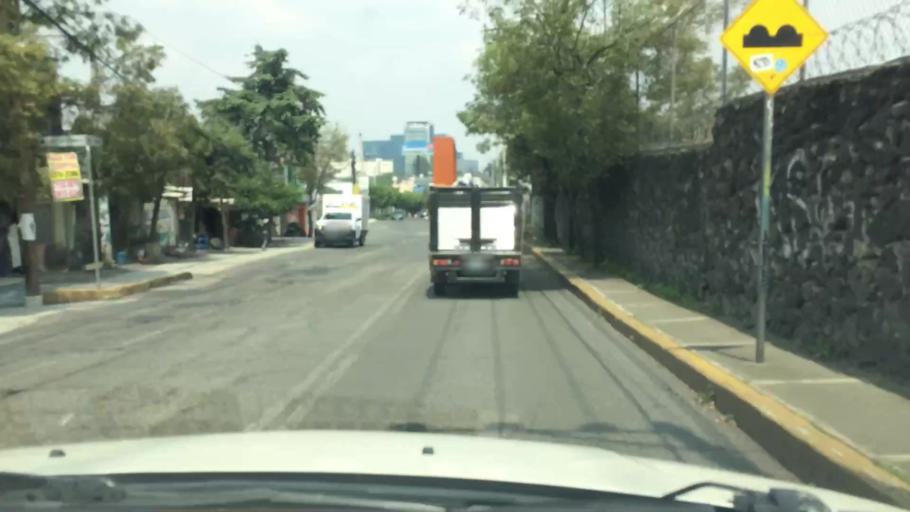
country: MX
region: Mexico City
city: Magdalena Contreras
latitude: 19.3032
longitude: -99.2208
